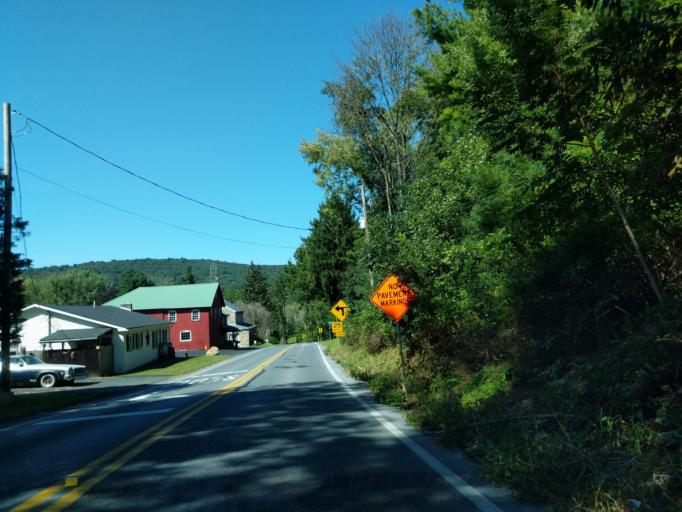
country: US
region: Pennsylvania
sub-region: Montgomery County
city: East Greenville
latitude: 40.4526
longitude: -75.4964
